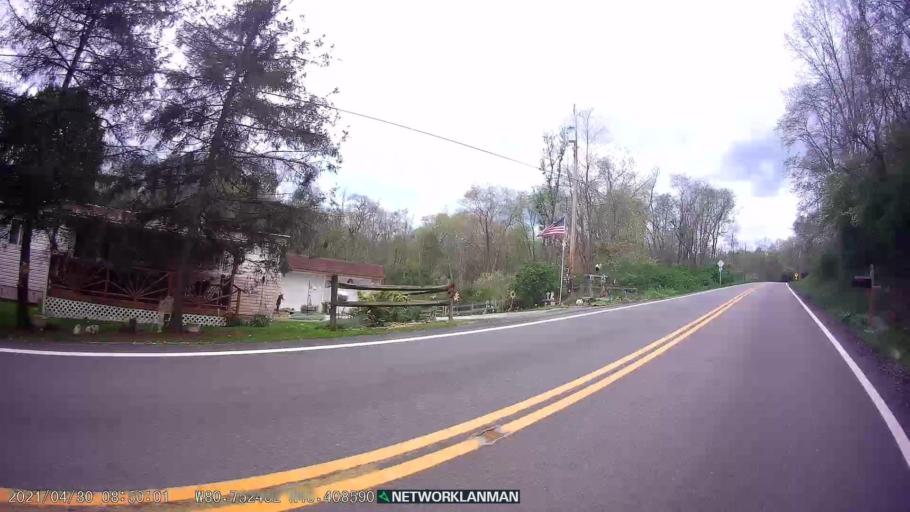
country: US
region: Ohio
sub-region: Jefferson County
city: Wintersville
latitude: 40.4088
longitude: -80.7526
